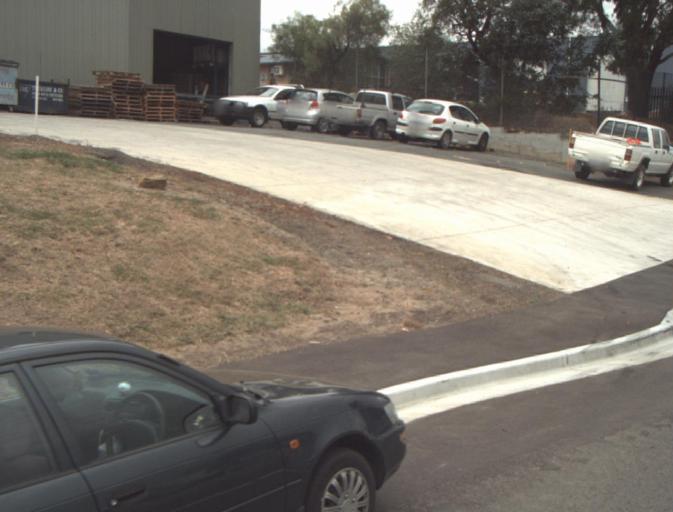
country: AU
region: Tasmania
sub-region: Launceston
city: Newstead
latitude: -41.4399
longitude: 147.1791
